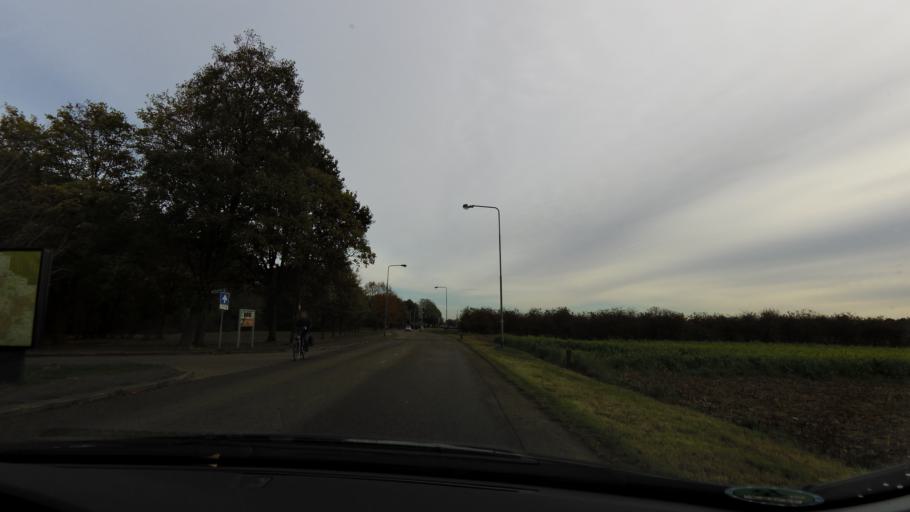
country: NL
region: Limburg
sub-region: Gemeente Sittard-Geleen
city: Born
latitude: 51.0426
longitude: 5.8168
